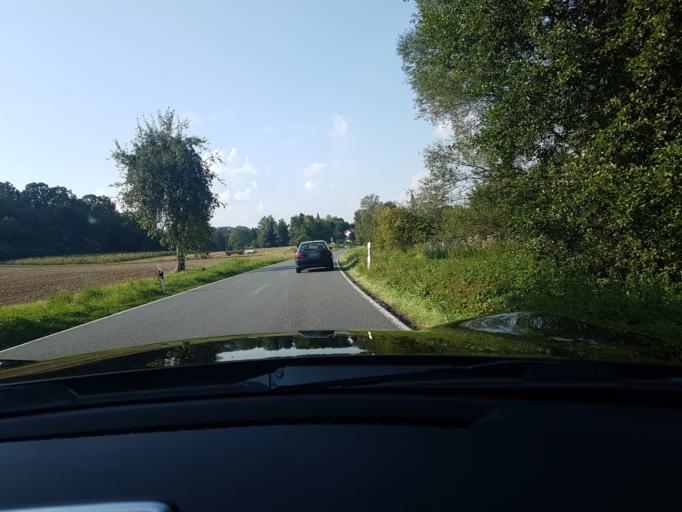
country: DE
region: Baden-Wuerttemberg
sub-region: Karlsruhe Region
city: Seckach
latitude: 49.4486
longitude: 9.3684
